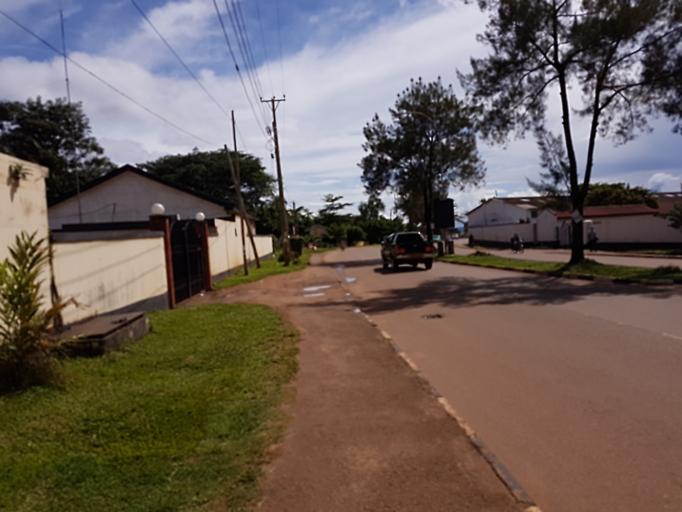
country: UG
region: Central Region
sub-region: Wakiso District
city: Entebbe
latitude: 0.0563
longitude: 32.4671
